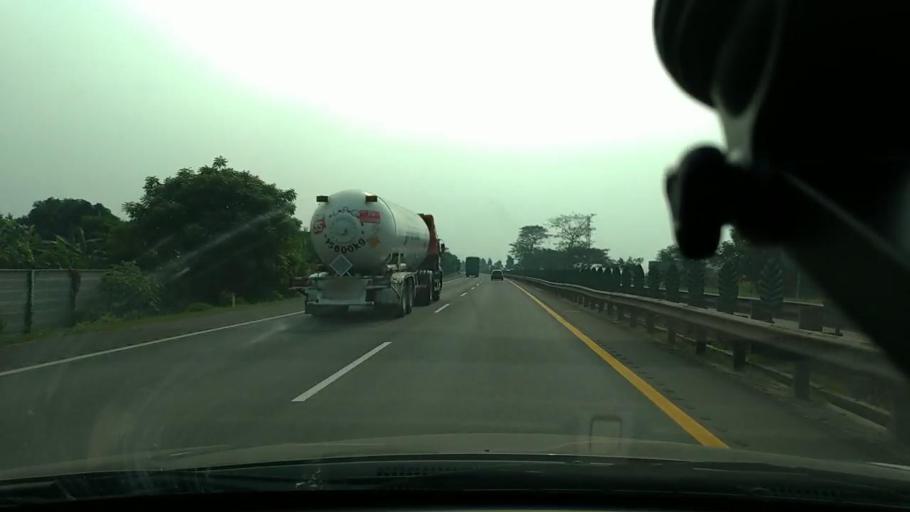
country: ID
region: Banten
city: Serang
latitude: -6.0974
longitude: 106.1678
